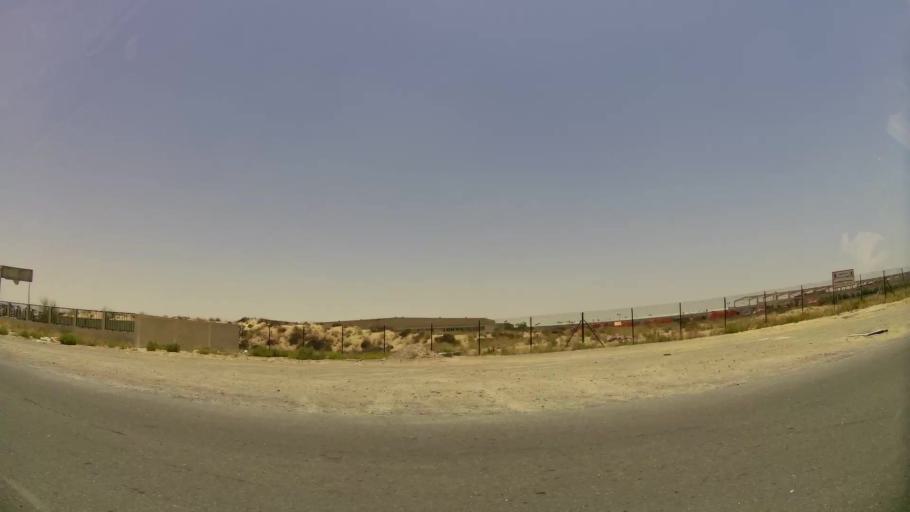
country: AE
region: Dubai
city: Dubai
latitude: 24.9852
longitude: 55.1659
